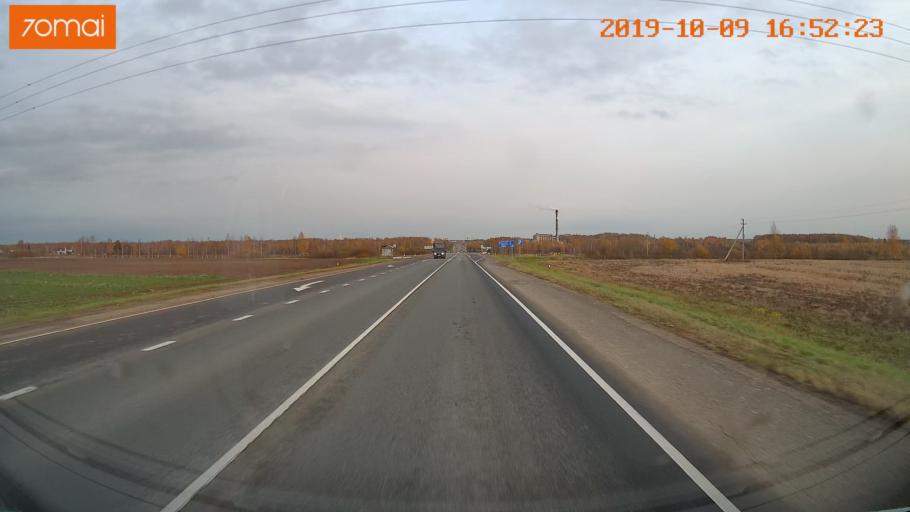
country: RU
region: Ivanovo
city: Privolzhsk
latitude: 57.3810
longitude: 41.2453
